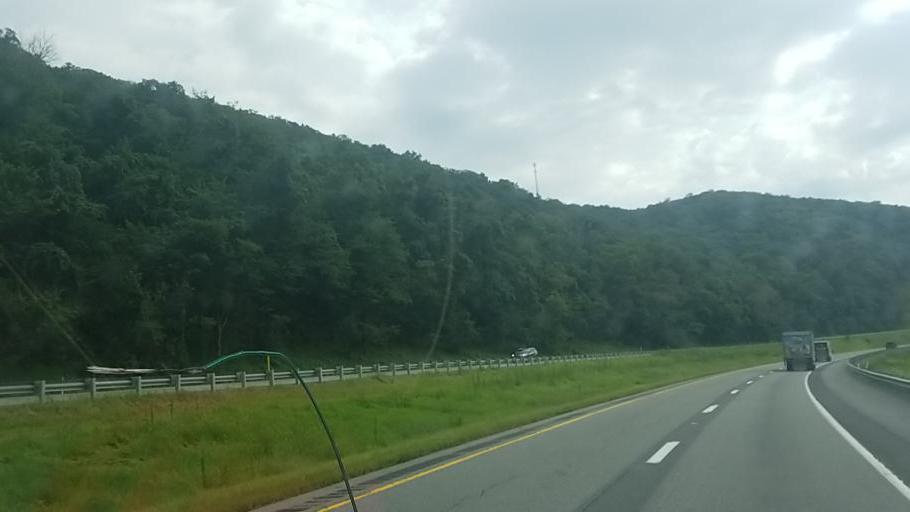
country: US
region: Pennsylvania
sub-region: Perry County
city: Newport
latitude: 40.5654
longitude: -77.1755
